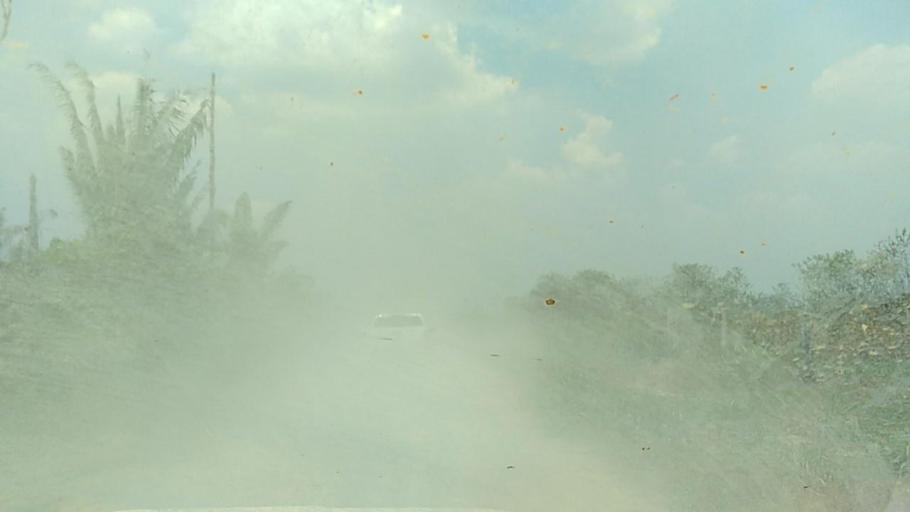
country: BR
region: Rondonia
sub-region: Porto Velho
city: Porto Velho
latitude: -8.7730
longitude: -63.2159
